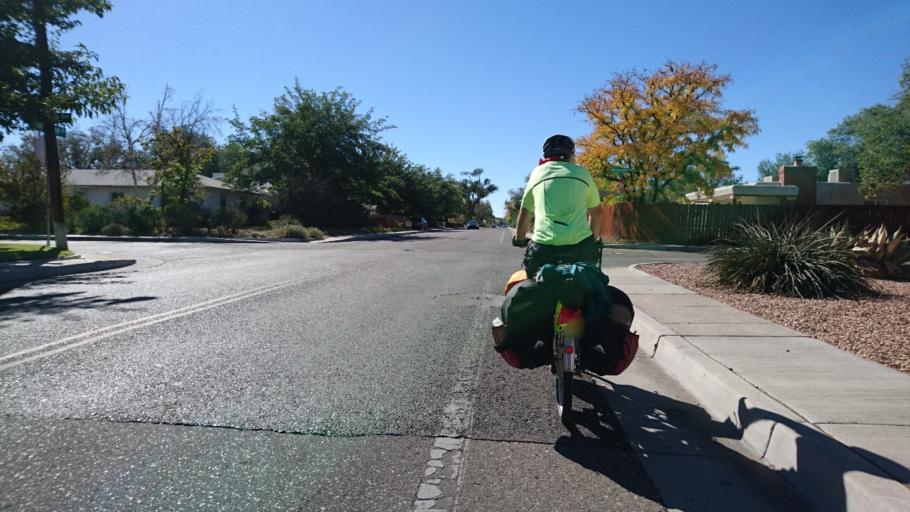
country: US
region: New Mexico
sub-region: Bernalillo County
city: Albuquerque
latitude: 35.0839
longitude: -106.5954
